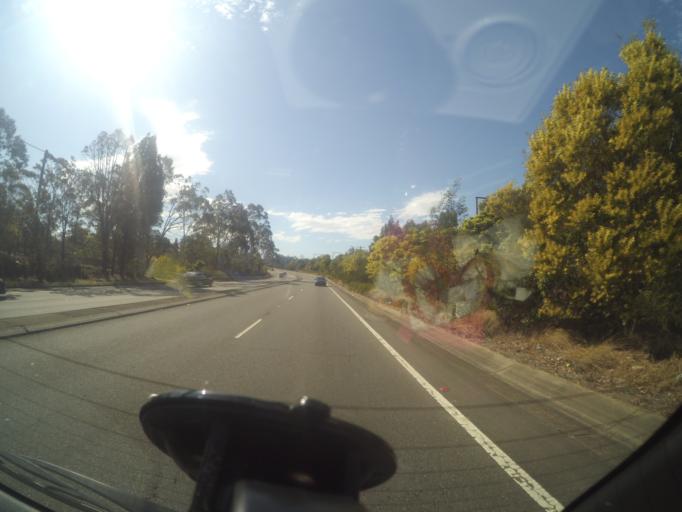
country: AU
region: New South Wales
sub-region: Blue Mountains Municipality
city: Hazelbrook
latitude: -33.7007
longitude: 150.5323
